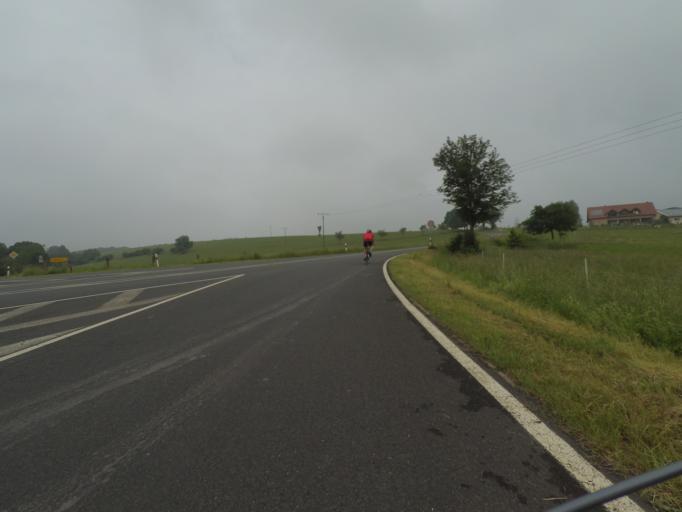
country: DE
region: Rheinland-Pfalz
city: Ernst
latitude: 50.1489
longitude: 7.2586
